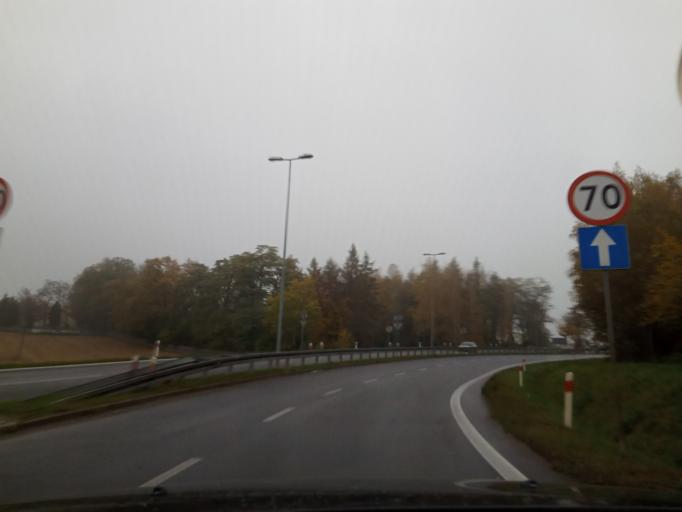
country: PL
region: Lesser Poland Voivodeship
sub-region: Powiat wielicki
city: Kokotow
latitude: 50.1148
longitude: 20.0867
